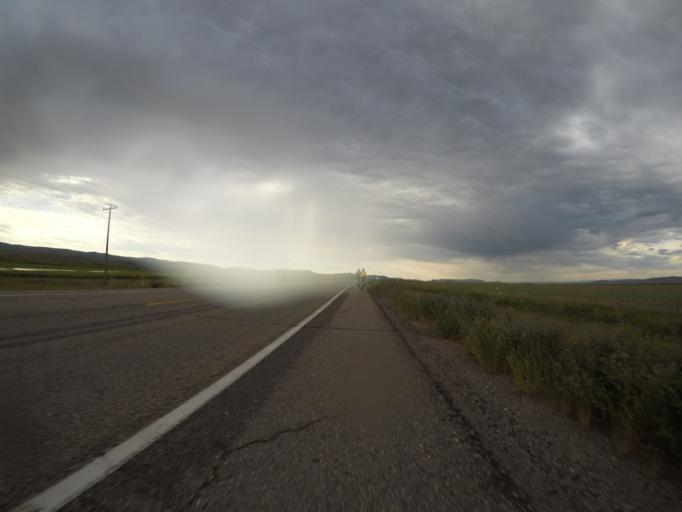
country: US
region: Utah
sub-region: Rich County
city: Randolph
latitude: 41.9402
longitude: -110.9529
